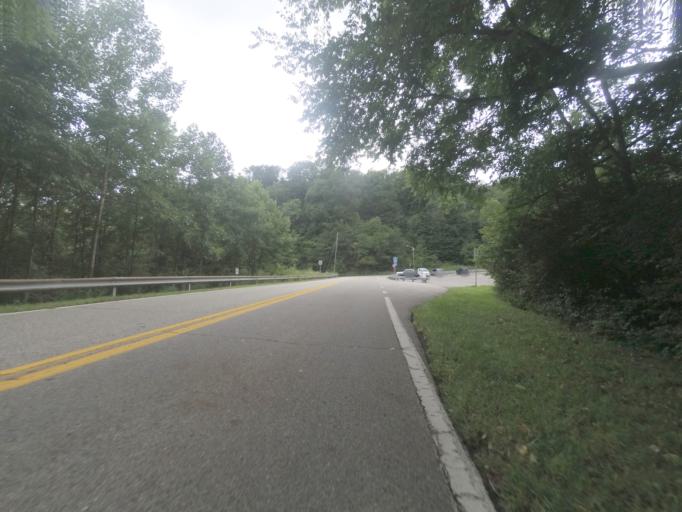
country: US
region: West Virginia
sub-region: Cabell County
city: Huntington
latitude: 38.3969
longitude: -82.4486
